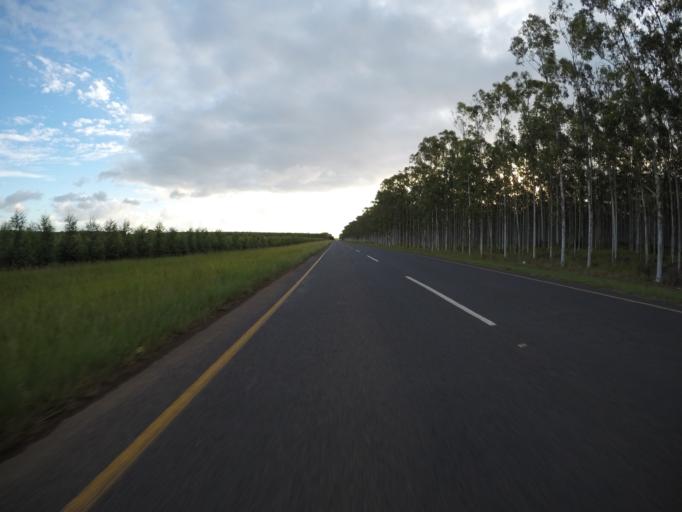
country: ZA
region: KwaZulu-Natal
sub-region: uMkhanyakude District Municipality
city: Mtubatuba
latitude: -28.4026
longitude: 32.2058
